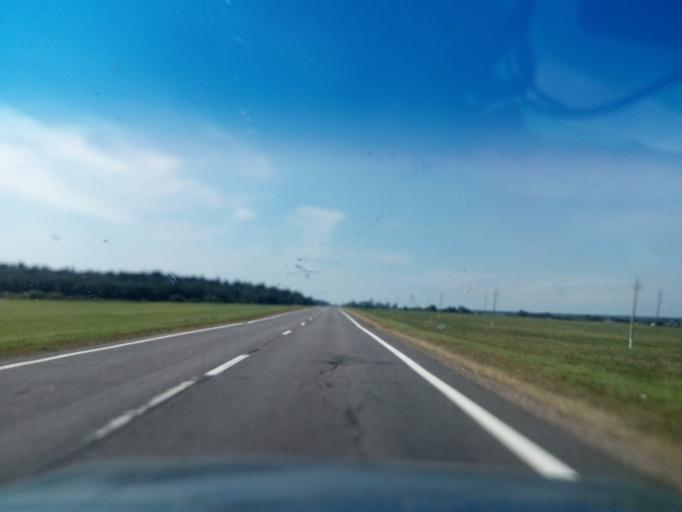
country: BY
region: Vitebsk
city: Vyerkhnyadzvinsk
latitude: 55.8233
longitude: 27.7573
